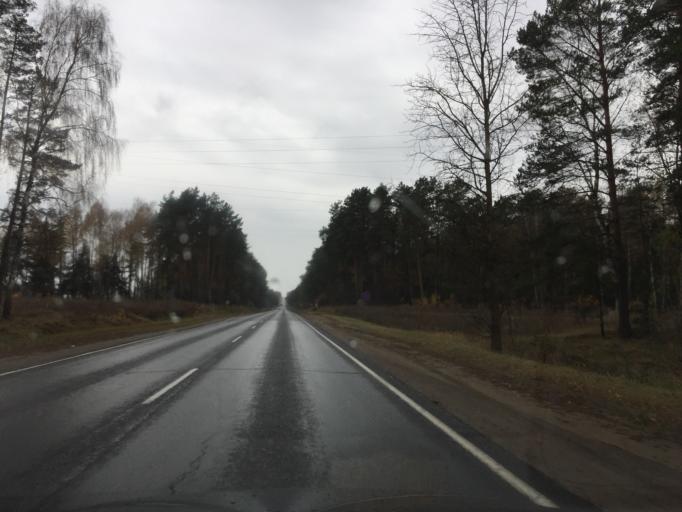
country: BY
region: Mogilev
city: Slawharad
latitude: 53.4118
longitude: 30.9444
